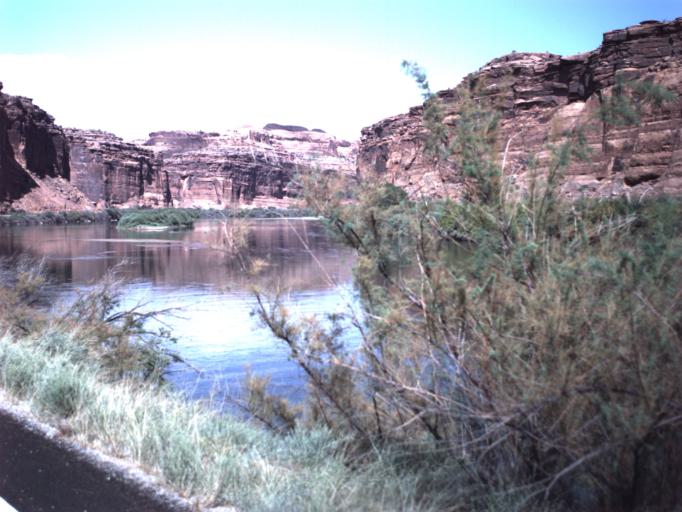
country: US
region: Utah
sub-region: Grand County
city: Moab
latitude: 38.5621
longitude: -109.6584
